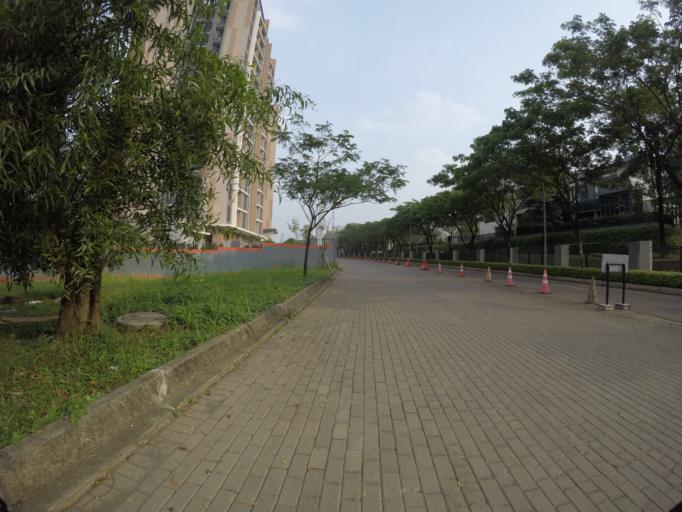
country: ID
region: West Java
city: Serpong
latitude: -6.2951
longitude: 106.6502
